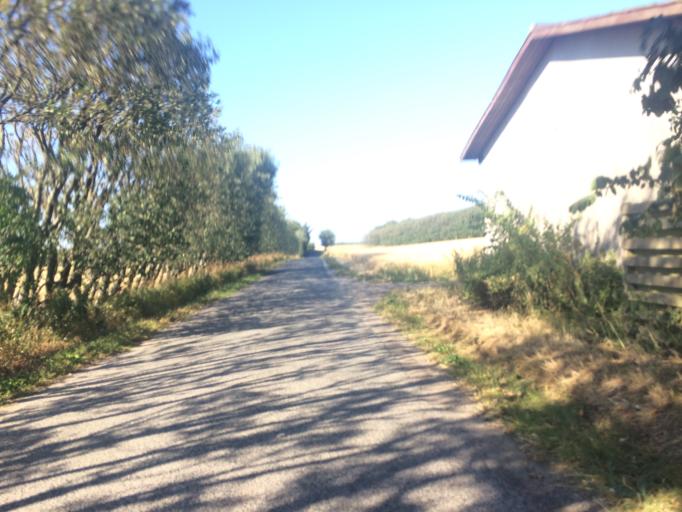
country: DK
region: Central Jutland
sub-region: Holstebro Kommune
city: Vinderup
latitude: 56.5838
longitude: 8.7310
